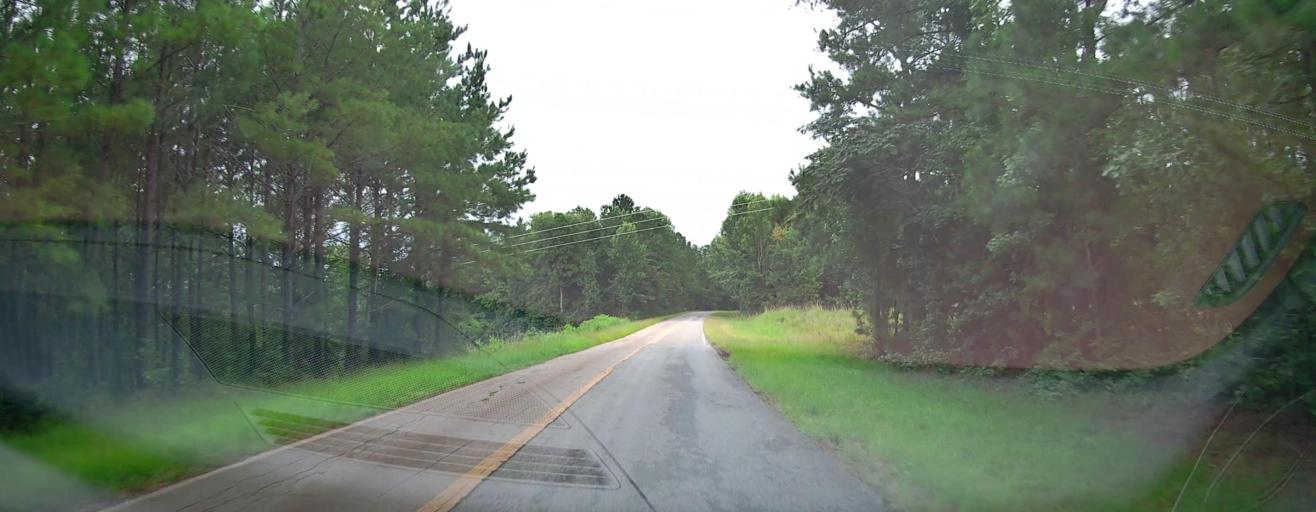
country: US
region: Georgia
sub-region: Bibb County
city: Macon
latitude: 32.7872
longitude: -83.5131
